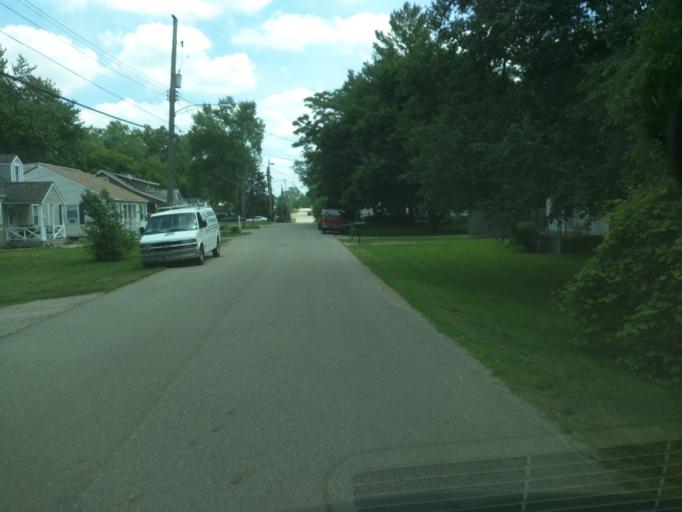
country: US
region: Michigan
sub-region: Ingham County
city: Lansing
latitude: 42.7637
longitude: -84.5459
